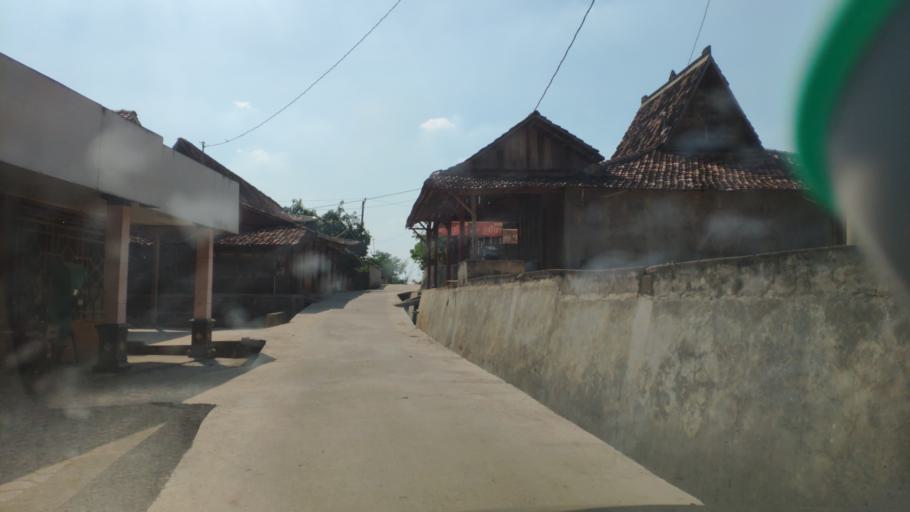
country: ID
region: Central Java
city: Ngapus
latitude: -6.9383
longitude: 111.2096
